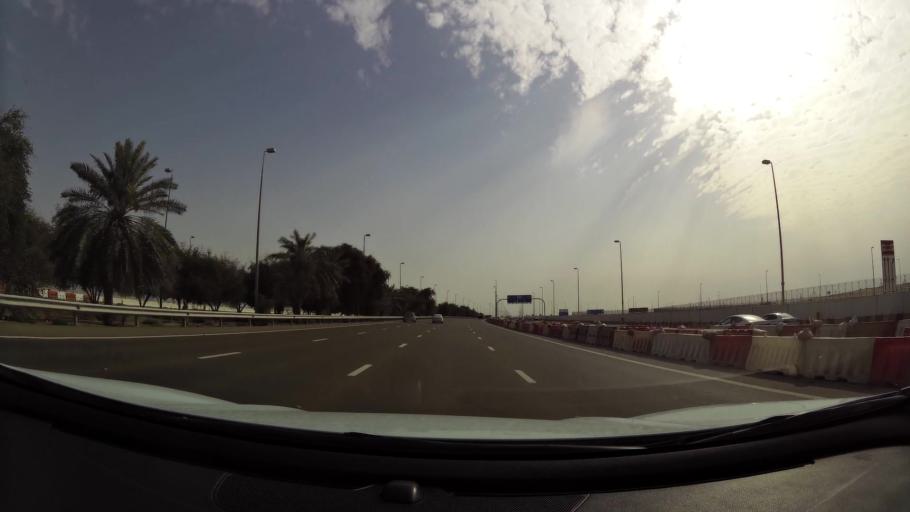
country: AE
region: Abu Dhabi
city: Abu Dhabi
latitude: 24.4180
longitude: 54.6765
